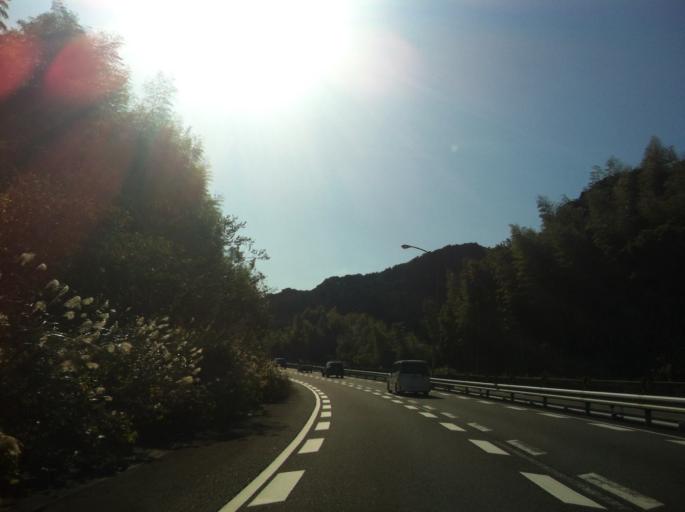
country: JP
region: Shizuoka
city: Yaizu
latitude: 34.9221
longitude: 138.2920
